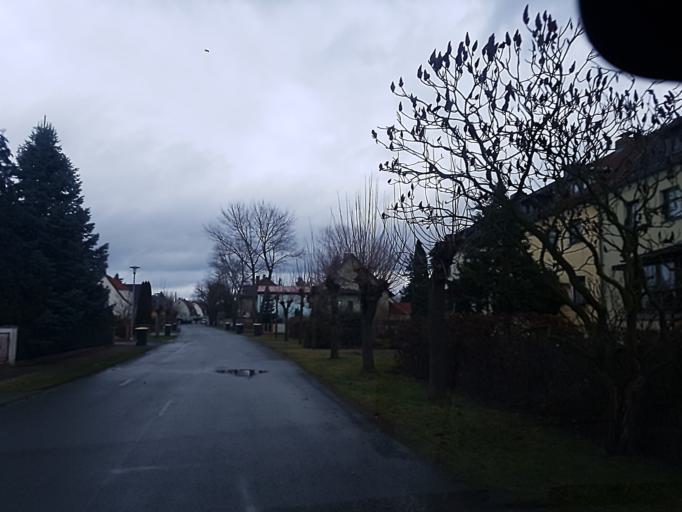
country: DE
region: Brandenburg
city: Bad Liebenwerda
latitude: 51.5096
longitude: 13.3962
